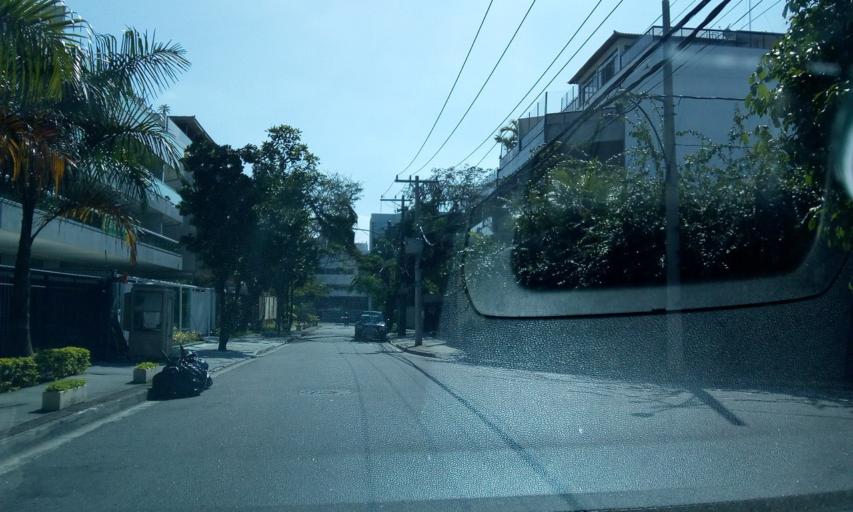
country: BR
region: Rio de Janeiro
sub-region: Nilopolis
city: Nilopolis
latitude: -23.0186
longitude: -43.4555
